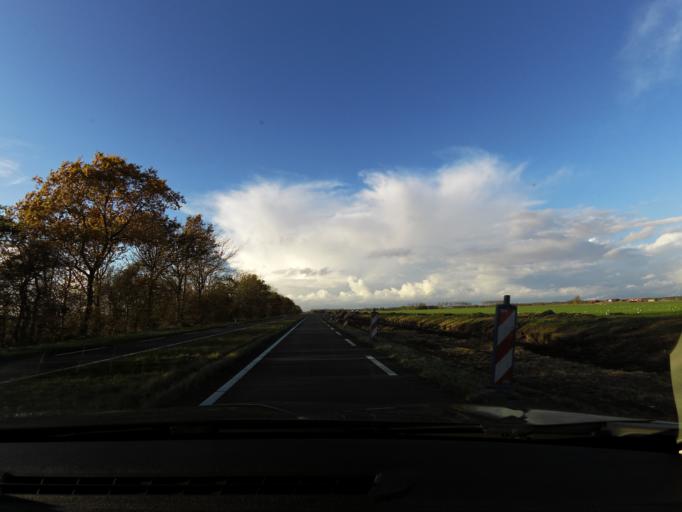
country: NL
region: South Holland
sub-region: Gemeente Goeree-Overflakkee
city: Dirksland
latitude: 51.7843
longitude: 4.0464
